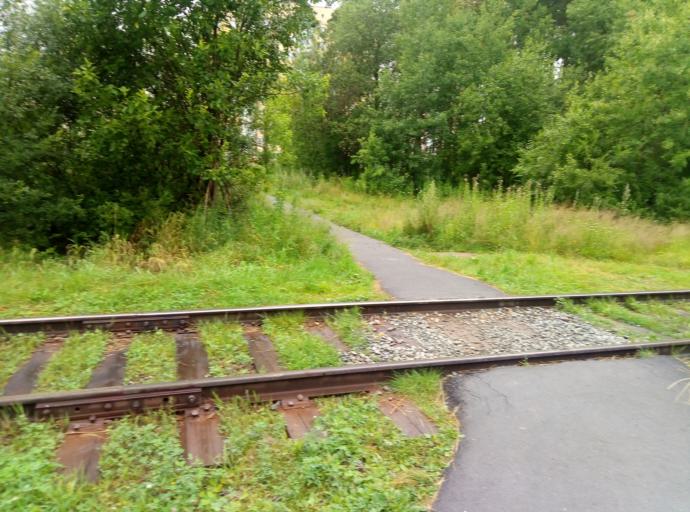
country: RU
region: Sverdlovsk
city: Beryozovsky
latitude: 56.9013
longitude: 60.7534
